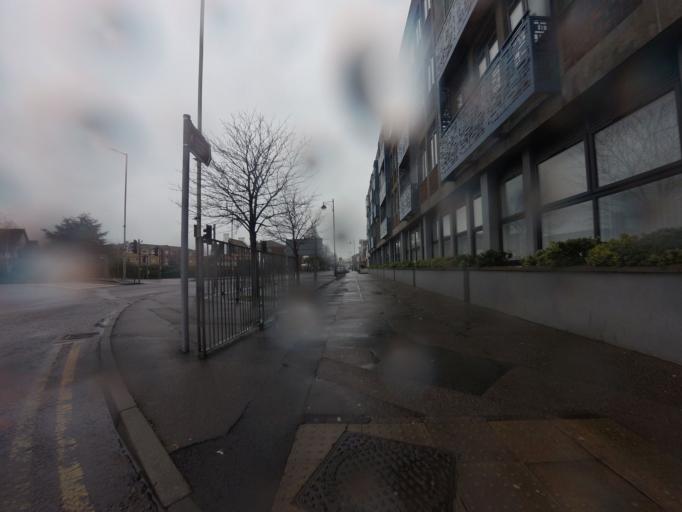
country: GB
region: England
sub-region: Hertfordshire
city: Waltham Cross
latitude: 51.6894
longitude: -0.0334
